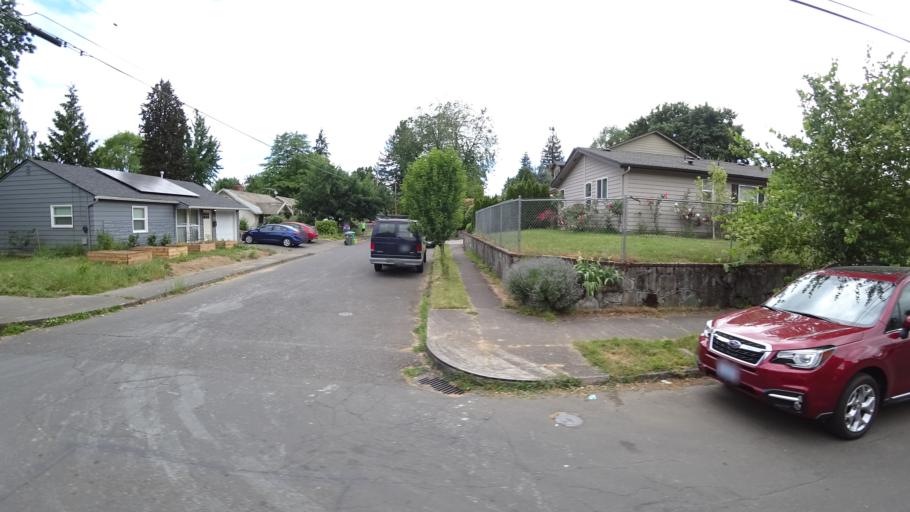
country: US
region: Oregon
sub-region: Washington County
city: West Haven
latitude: 45.5986
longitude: -122.7513
